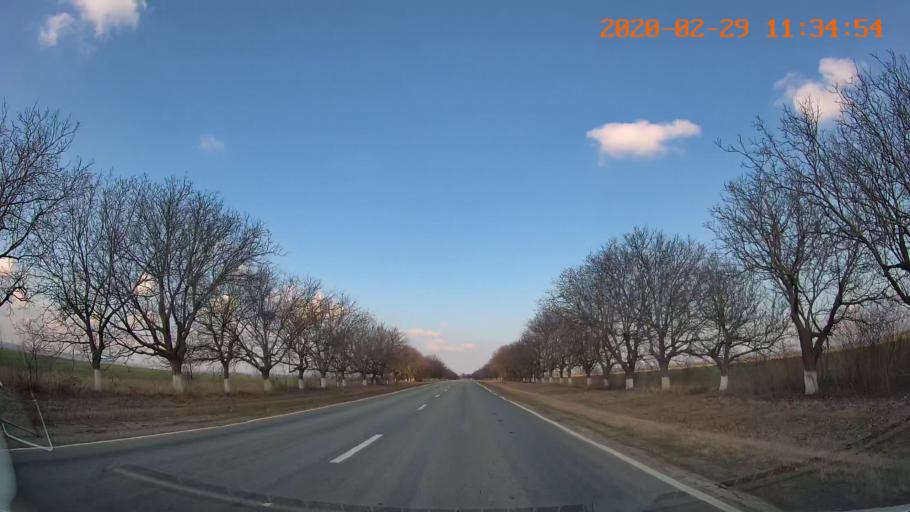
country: MD
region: Rezina
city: Saharna
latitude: 47.5723
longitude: 29.0689
